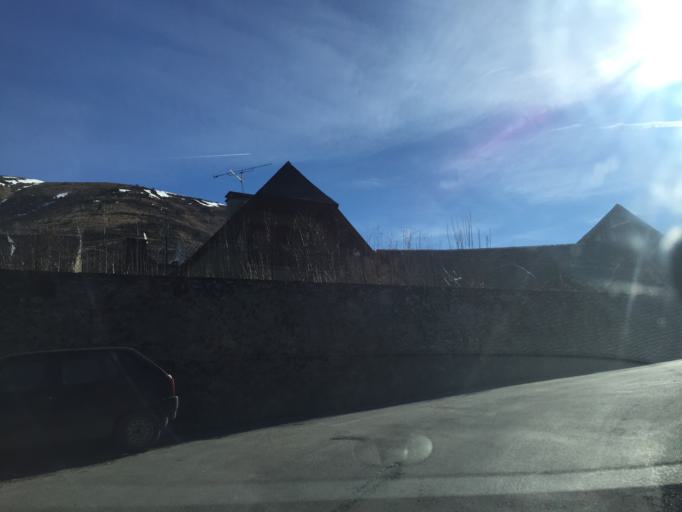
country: FR
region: Midi-Pyrenees
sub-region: Departement des Hautes-Pyrenees
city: Saint-Lary-Soulan
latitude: 42.8121
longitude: 0.3510
